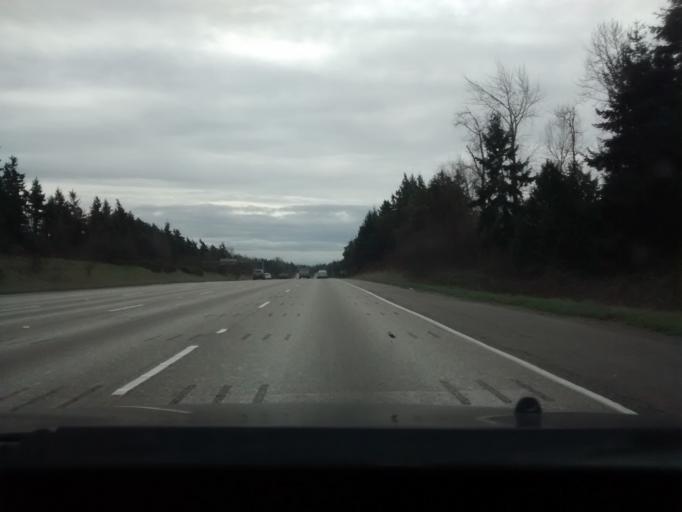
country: US
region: Washington
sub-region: King County
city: Des Moines
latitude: 47.3755
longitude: -122.2924
